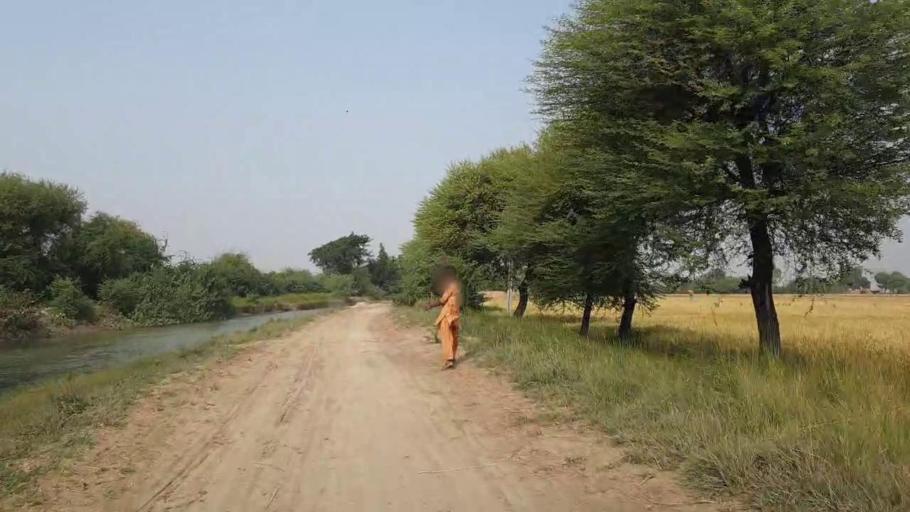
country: PK
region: Sindh
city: Kario
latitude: 24.8317
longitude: 68.5452
